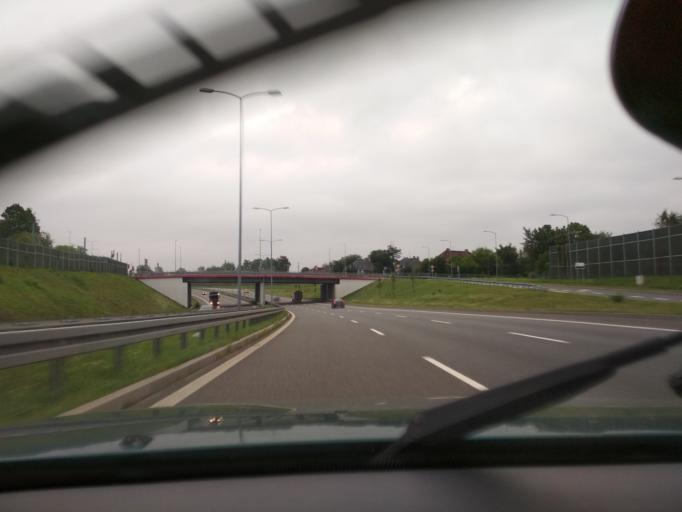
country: PL
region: Silesian Voivodeship
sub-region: Zabrze
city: Zabrze
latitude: 50.2931
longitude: 18.8121
